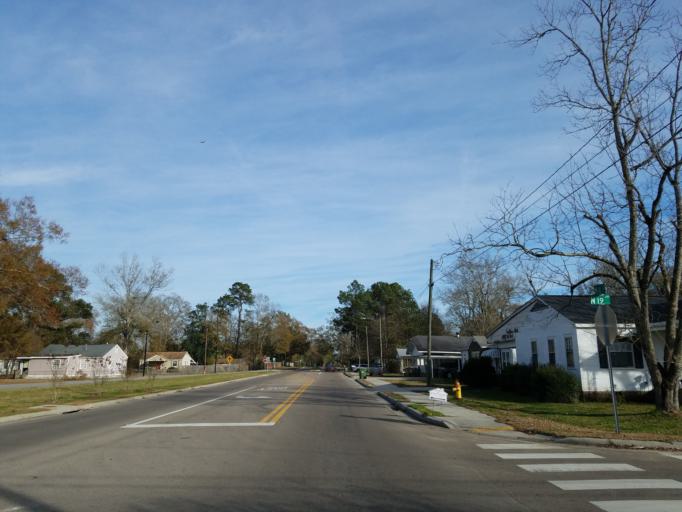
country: US
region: Mississippi
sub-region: Forrest County
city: Hattiesburg
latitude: 31.3320
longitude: -89.3191
